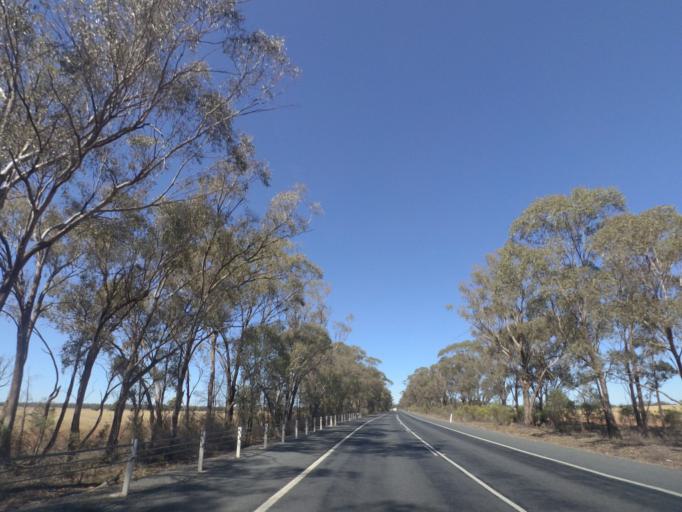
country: AU
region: New South Wales
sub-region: Bland
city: West Wyalong
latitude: -34.1145
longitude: 147.1365
